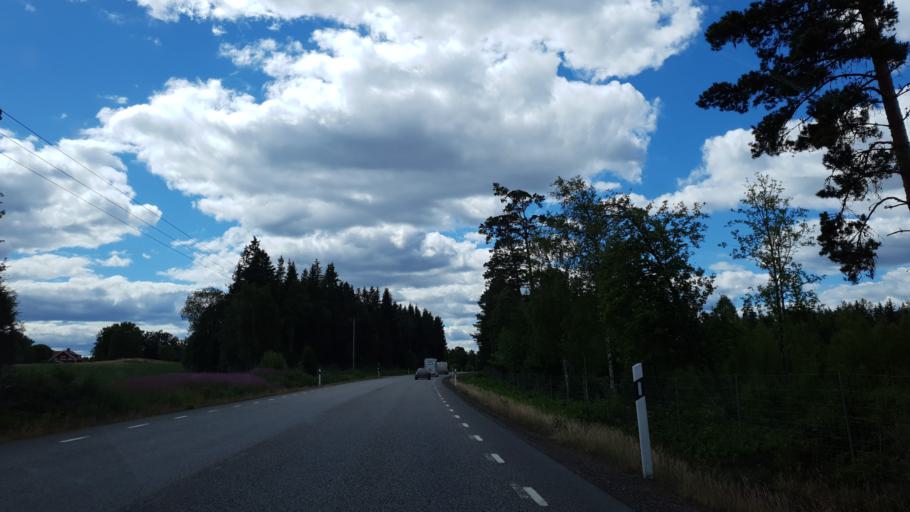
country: SE
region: Kronoberg
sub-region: Vaxjo Kommun
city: Braas
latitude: 57.1647
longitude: 15.1628
